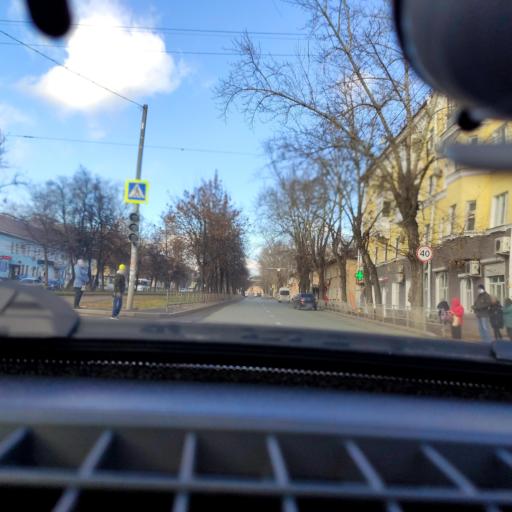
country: RU
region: Bashkortostan
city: Ufa
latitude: 54.8176
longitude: 56.1024
